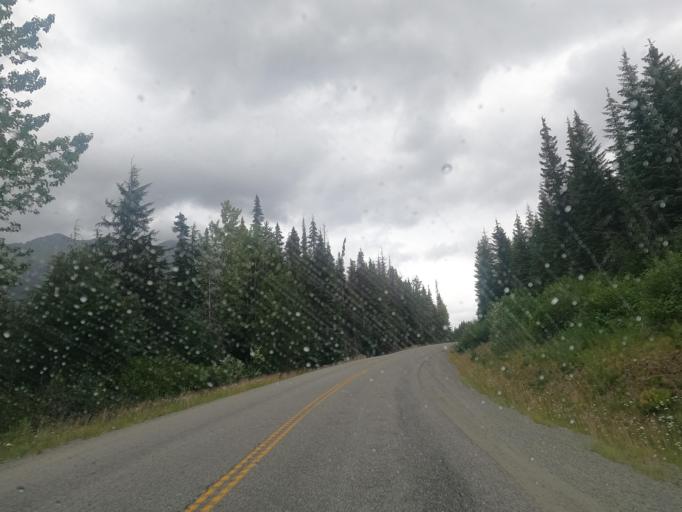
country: CA
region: British Columbia
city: Pemberton
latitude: 50.3886
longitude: -122.3468
